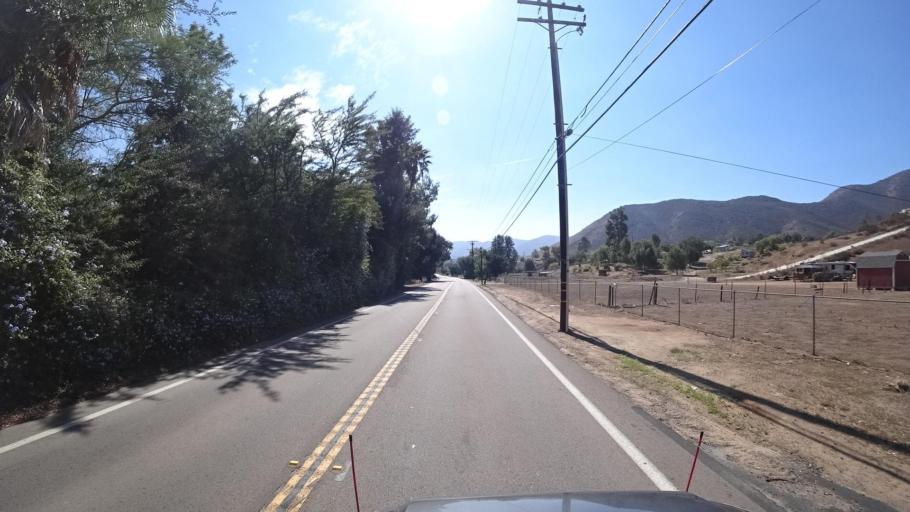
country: US
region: California
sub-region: San Diego County
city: Crest
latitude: 32.7954
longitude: -116.8461
